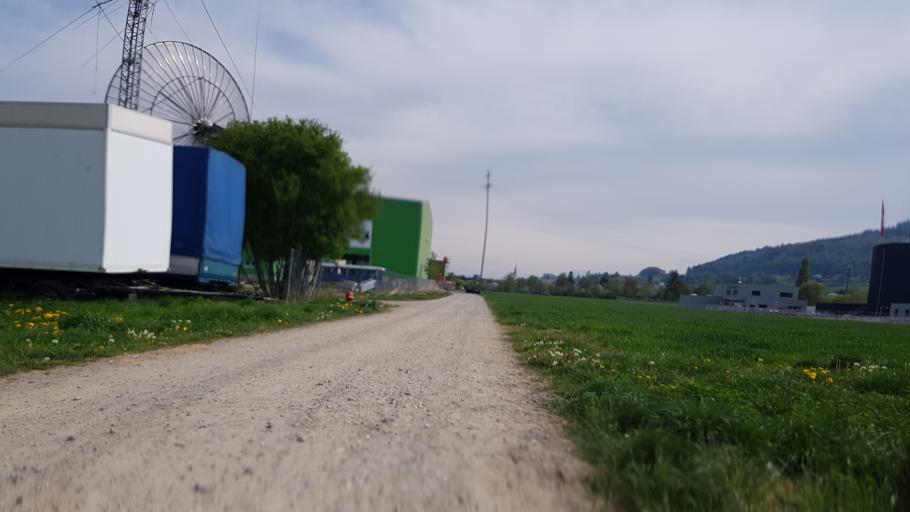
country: CH
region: Aargau
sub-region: Bezirk Kulm
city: Reinach
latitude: 47.2642
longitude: 8.1716
